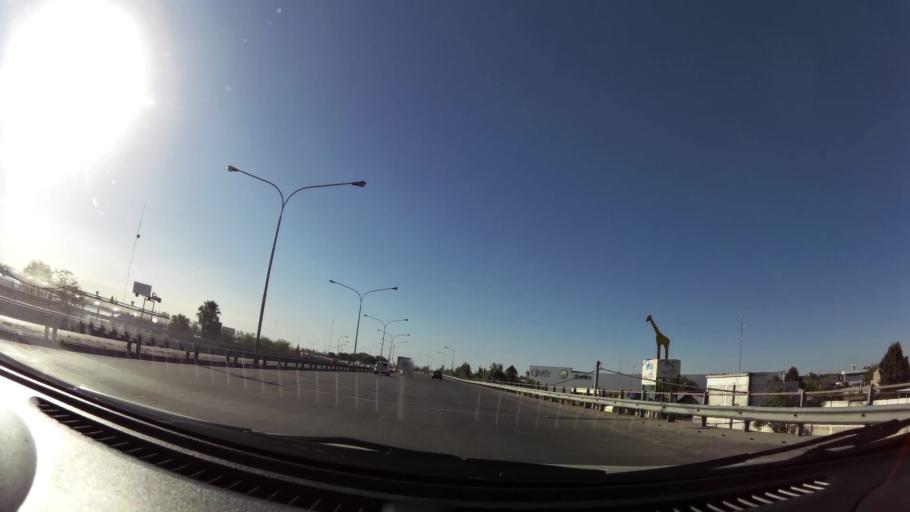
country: AR
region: Mendoza
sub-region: Departamento de Godoy Cruz
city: Godoy Cruz
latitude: -32.9243
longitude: -68.8360
